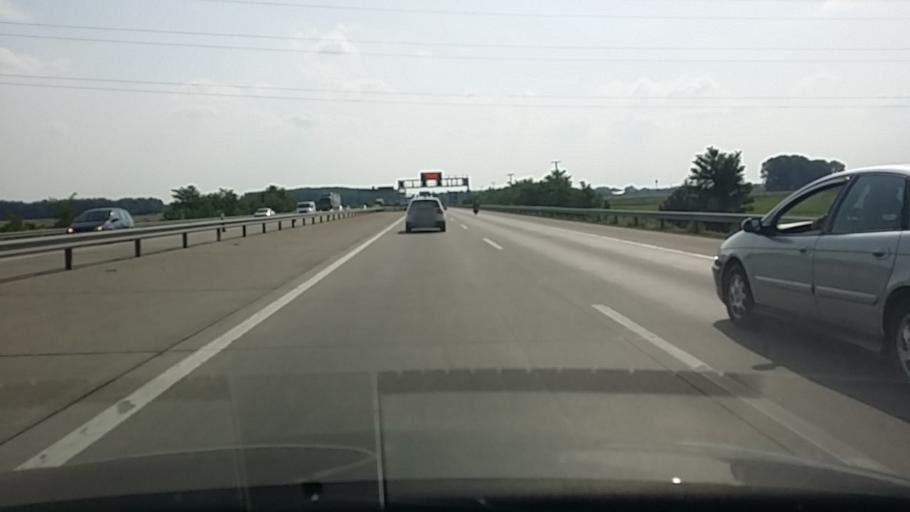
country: HU
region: Pest
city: Gyal
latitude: 47.3747
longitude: 19.2556
